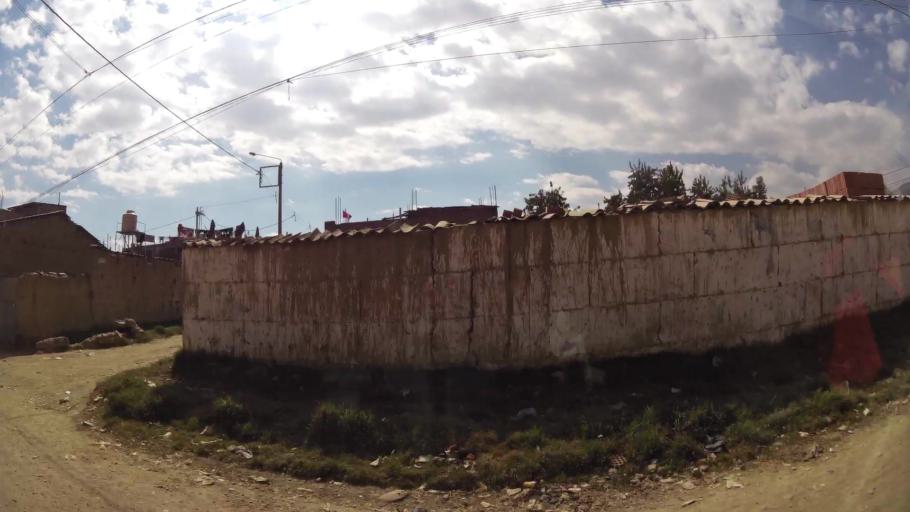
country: PE
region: Junin
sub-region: Provincia de Huancayo
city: Huancayo
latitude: -12.0932
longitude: -75.1993
